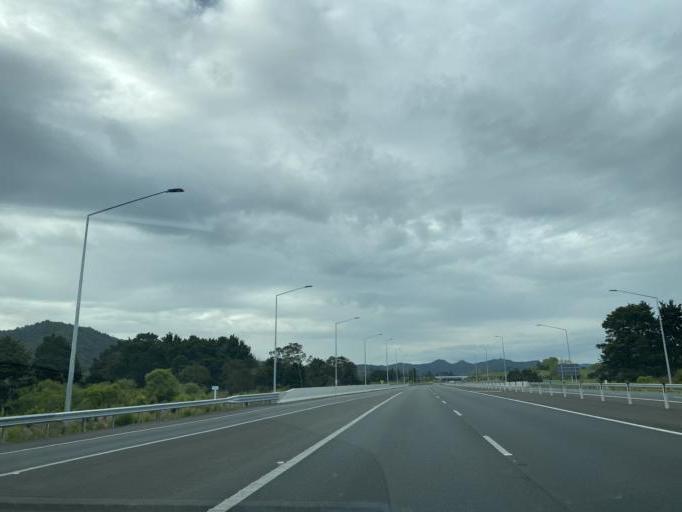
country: NZ
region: Waikato
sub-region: Waikato District
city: Ngaruawahia
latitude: -37.6196
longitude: 175.2052
